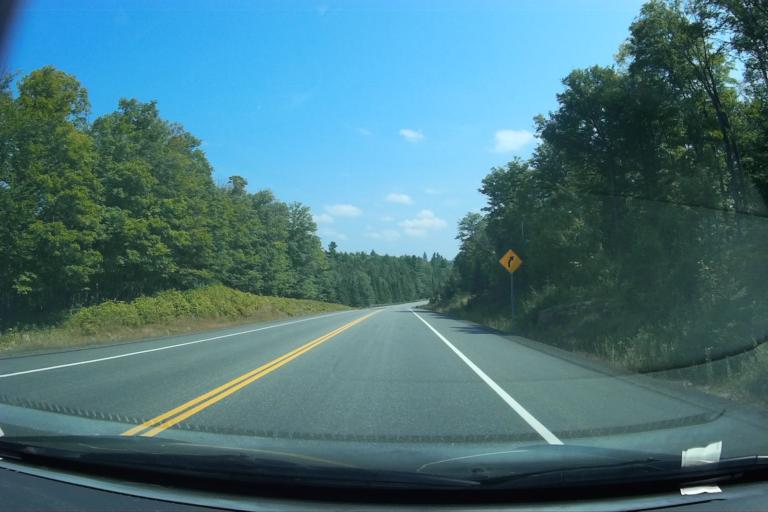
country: CA
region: Ontario
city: Huntsville
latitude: 45.5436
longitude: -78.6770
